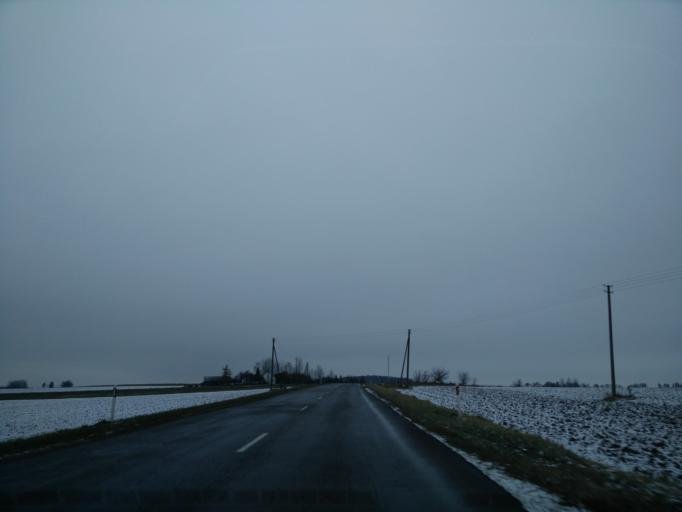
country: LT
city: Ariogala
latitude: 55.3373
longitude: 23.4011
